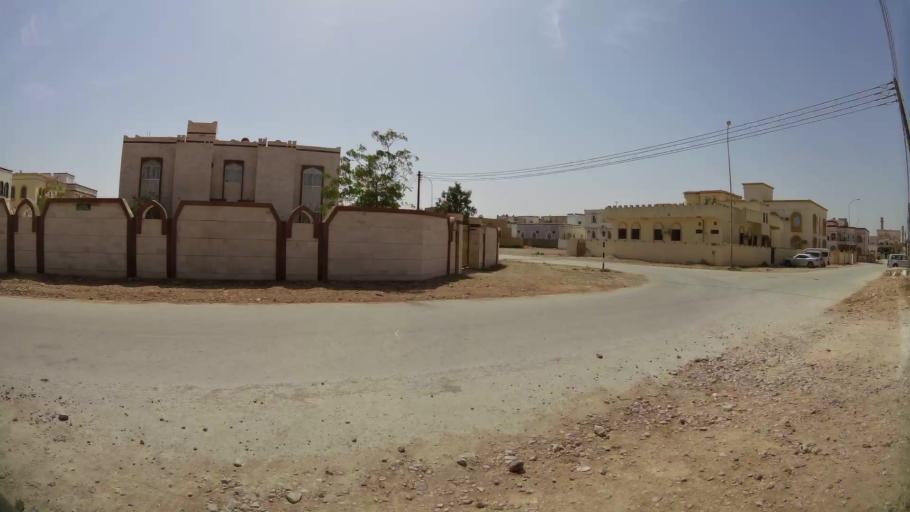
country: OM
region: Zufar
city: Salalah
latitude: 17.0478
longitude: 54.1606
